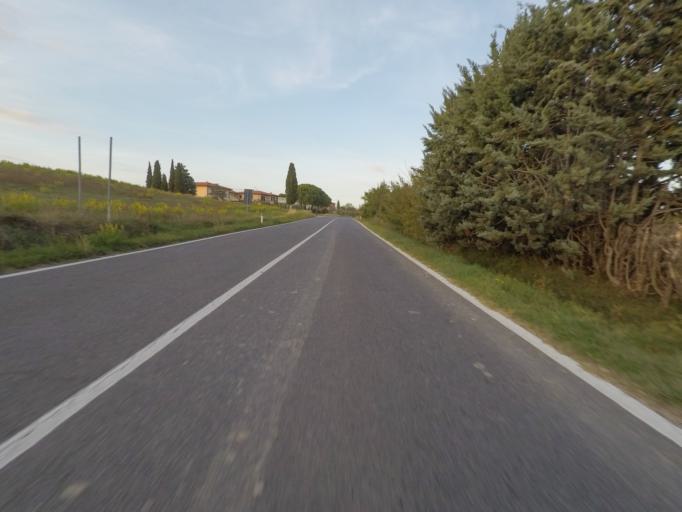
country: IT
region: Tuscany
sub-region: Provincia di Siena
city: Pienza
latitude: 43.0862
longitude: 11.6786
